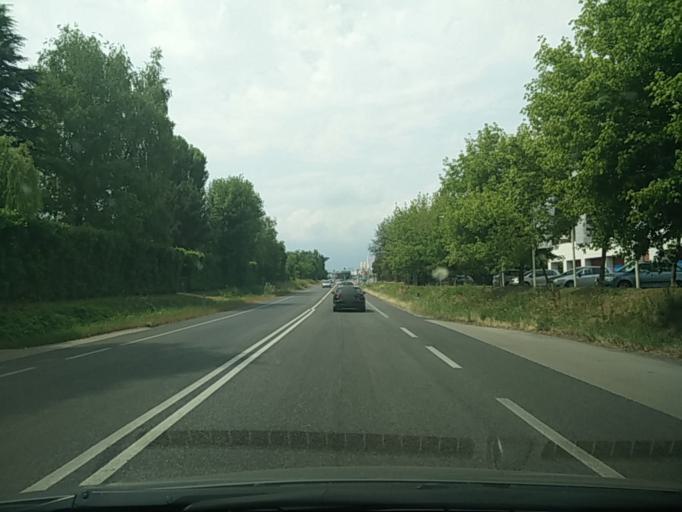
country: IT
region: Friuli Venezia Giulia
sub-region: Provincia di Pordenone
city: Pordenone
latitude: 45.9702
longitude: 12.6664
